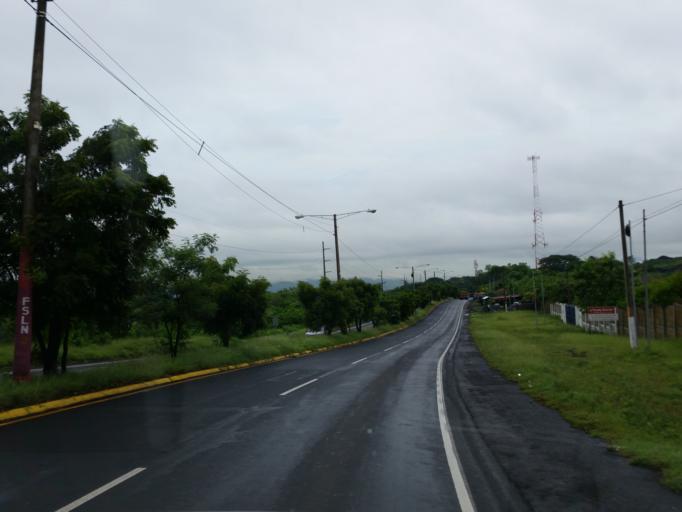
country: NI
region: Managua
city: Ciudad Sandino
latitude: 12.1349
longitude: -86.3260
